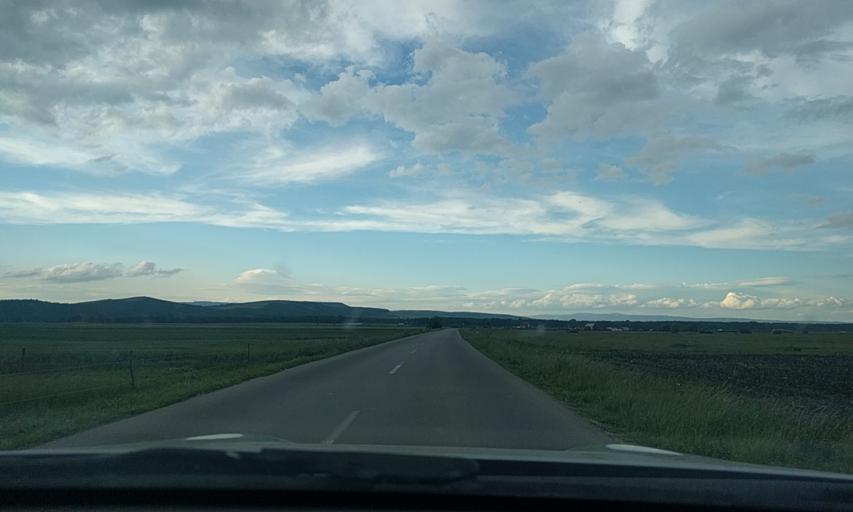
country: RO
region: Brasov
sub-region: Comuna Harman
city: Harman
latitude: 45.7285
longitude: 25.6995
